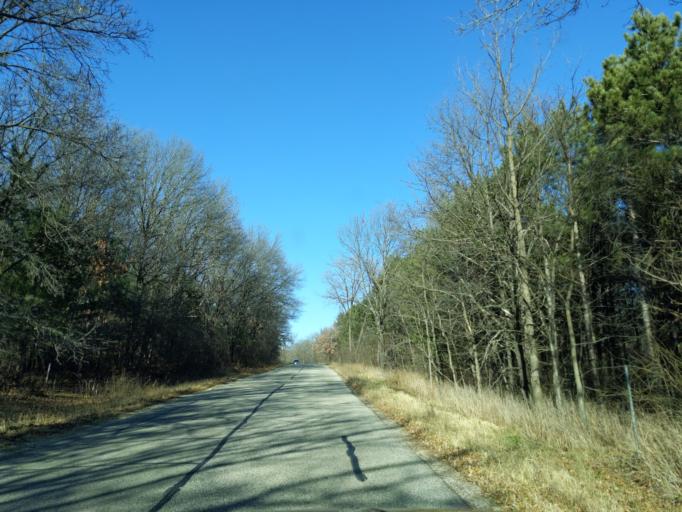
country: US
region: Wisconsin
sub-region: Waushara County
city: Wautoma
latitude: 44.1132
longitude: -89.2806
